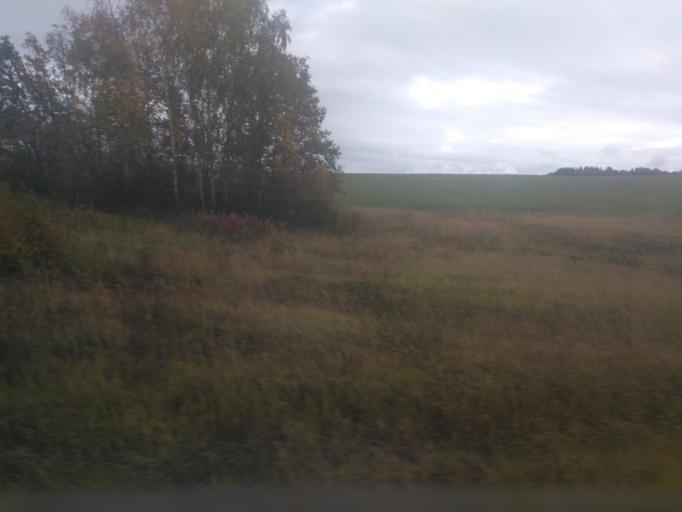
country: RU
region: Udmurtiya
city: Alnashi
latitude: 56.2351
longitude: 52.7278
